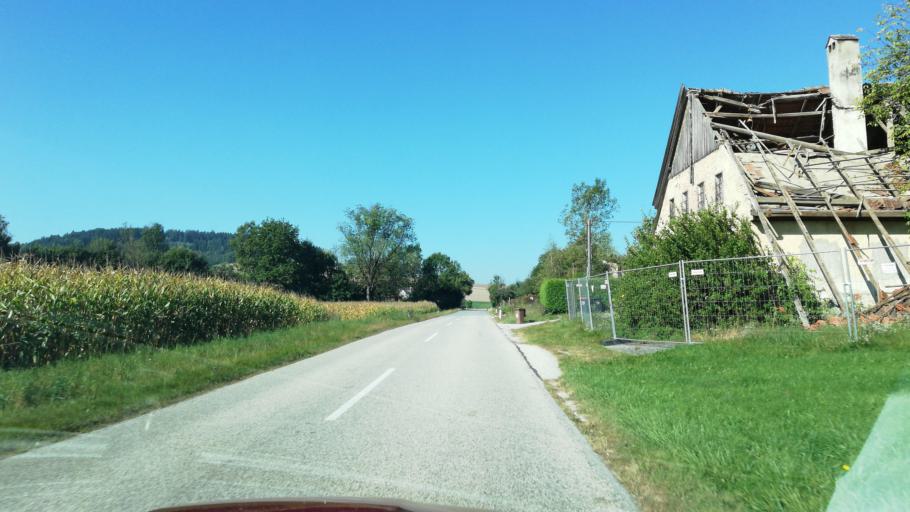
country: AT
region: Upper Austria
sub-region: Politischer Bezirk Grieskirchen
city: Bad Schallerbach
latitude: 48.1961
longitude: 13.8938
